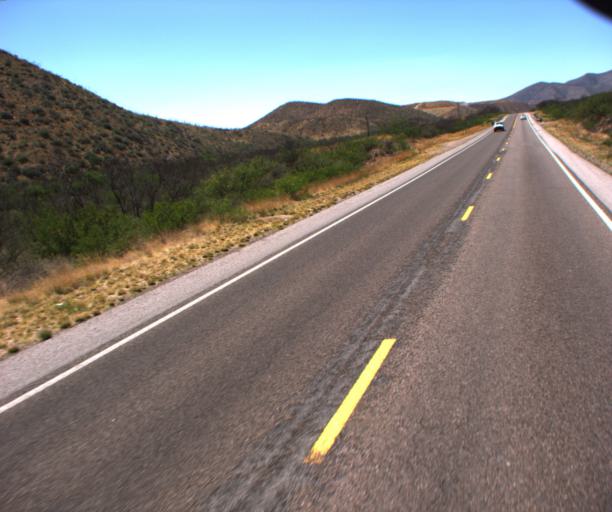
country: US
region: Arizona
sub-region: Cochise County
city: Bisbee
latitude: 31.4325
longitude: -109.8481
